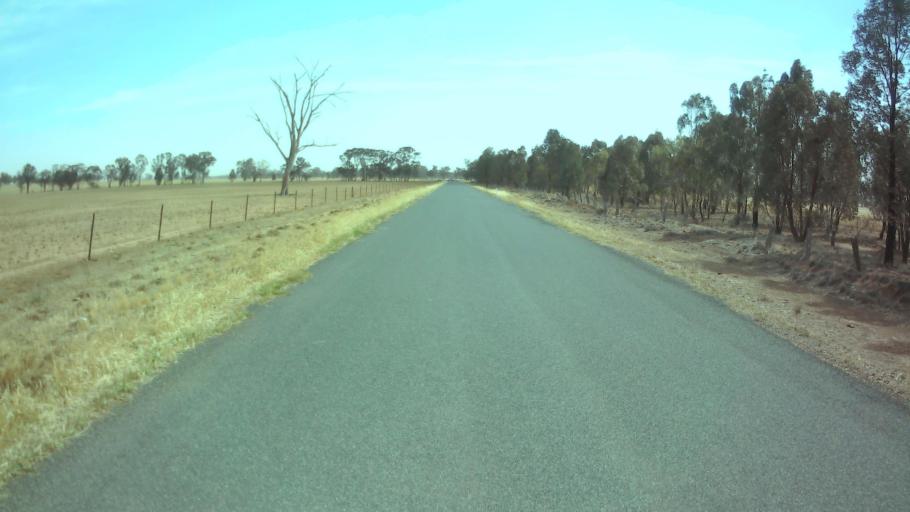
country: AU
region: New South Wales
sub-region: Weddin
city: Grenfell
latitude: -33.7133
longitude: 148.0013
